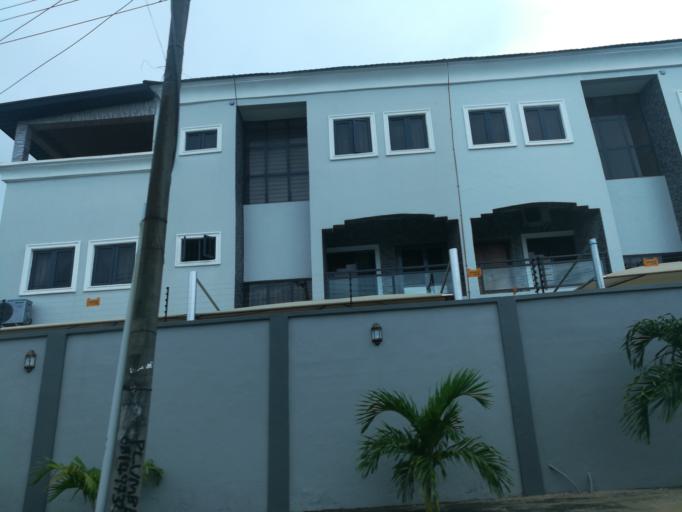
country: NG
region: Lagos
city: Ikoyi
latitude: 6.4457
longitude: 3.4766
